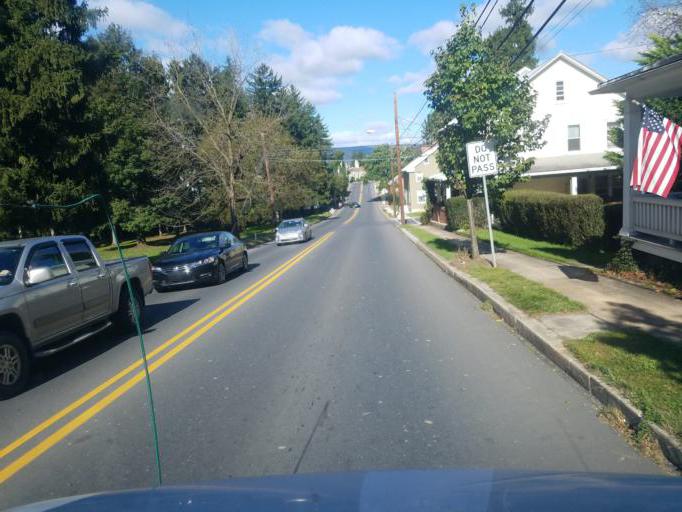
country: US
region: Pennsylvania
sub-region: Franklin County
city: Mercersburg
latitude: 39.8240
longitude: -77.9017
